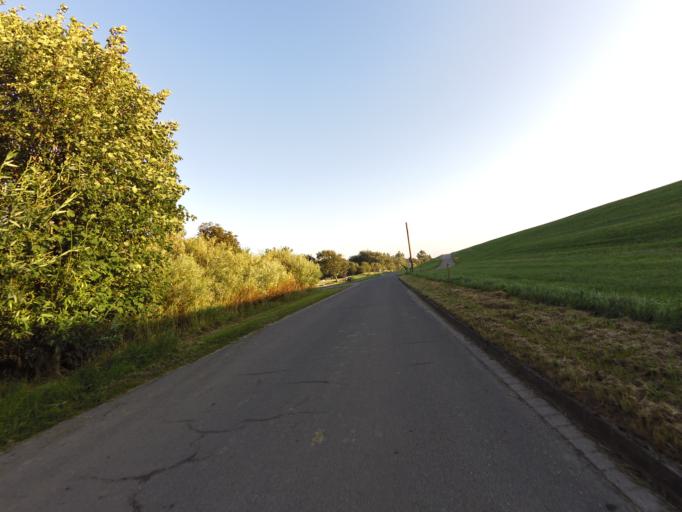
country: DE
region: Lower Saxony
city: Padingbuttel
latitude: 53.7459
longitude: 8.5277
